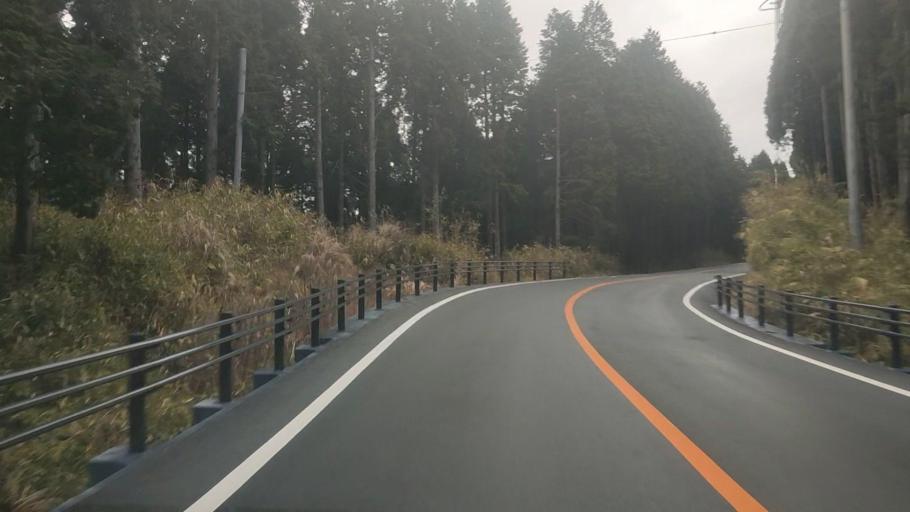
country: JP
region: Kumamoto
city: Aso
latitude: 32.8985
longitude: 131.0284
